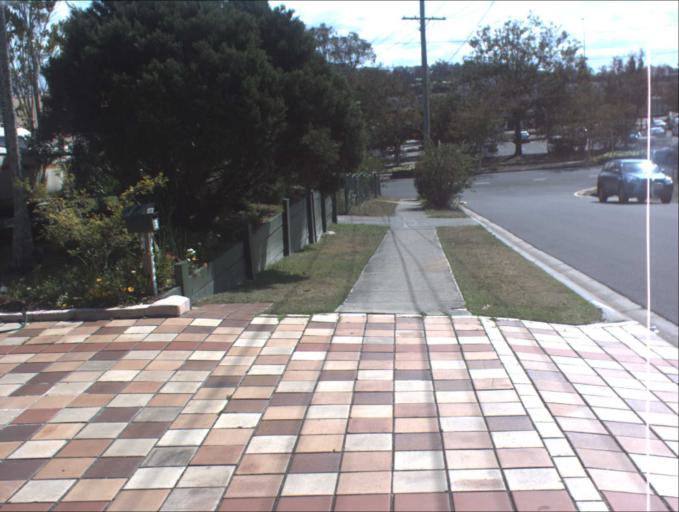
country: AU
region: Queensland
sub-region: Logan
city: Slacks Creek
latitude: -27.6601
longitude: 153.1749
